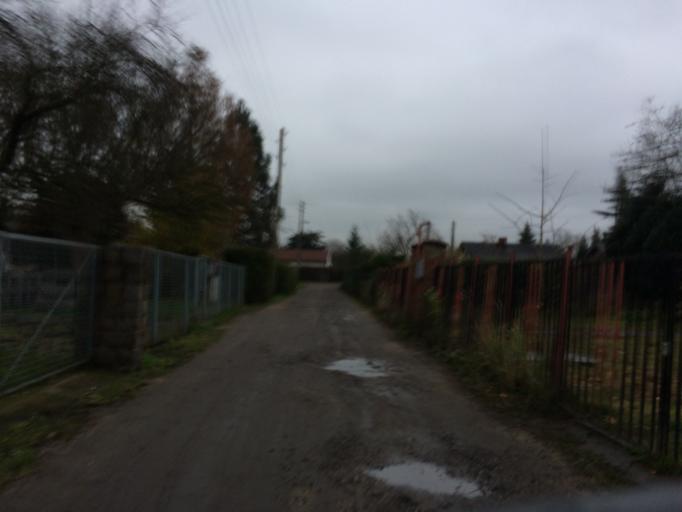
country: DE
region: Berlin
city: Blankenburg
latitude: 52.5864
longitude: 13.4429
